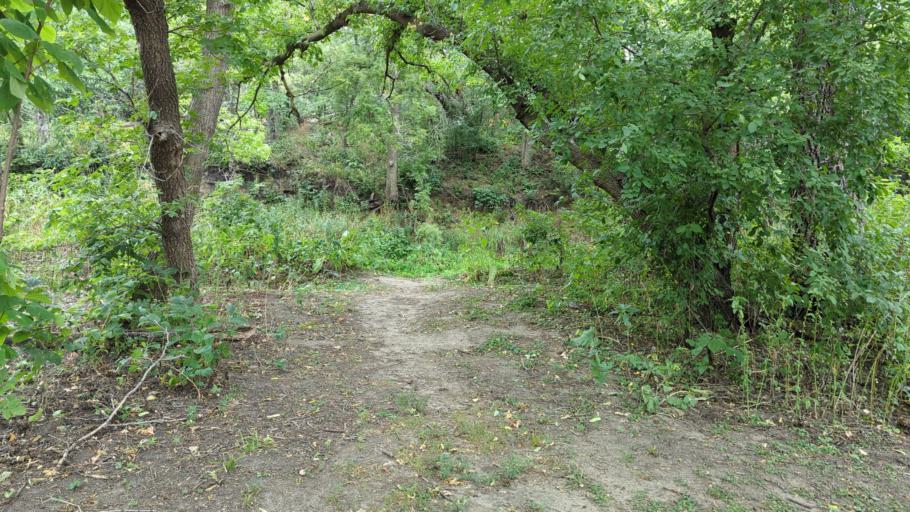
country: US
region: South Dakota
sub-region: Union County
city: Beresford
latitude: 42.9255
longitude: -96.7801
